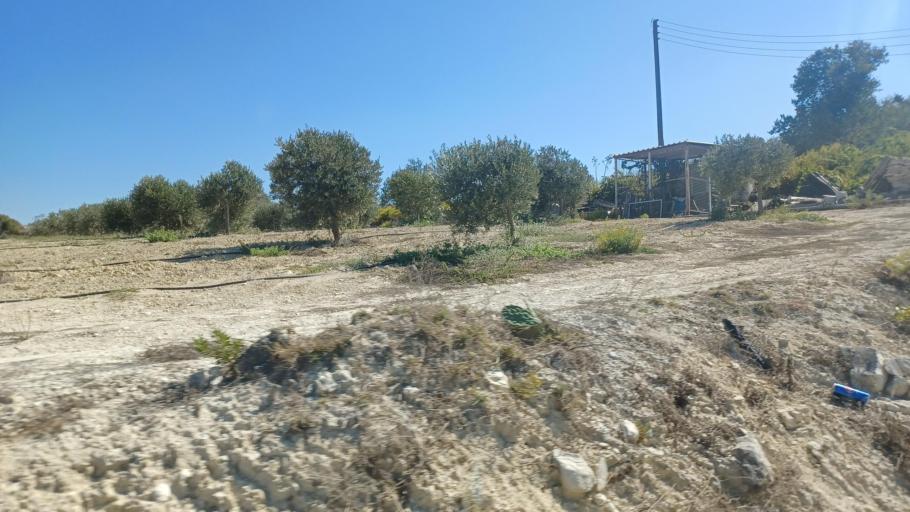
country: CY
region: Pafos
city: Mesogi
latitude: 34.8287
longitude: 32.4791
